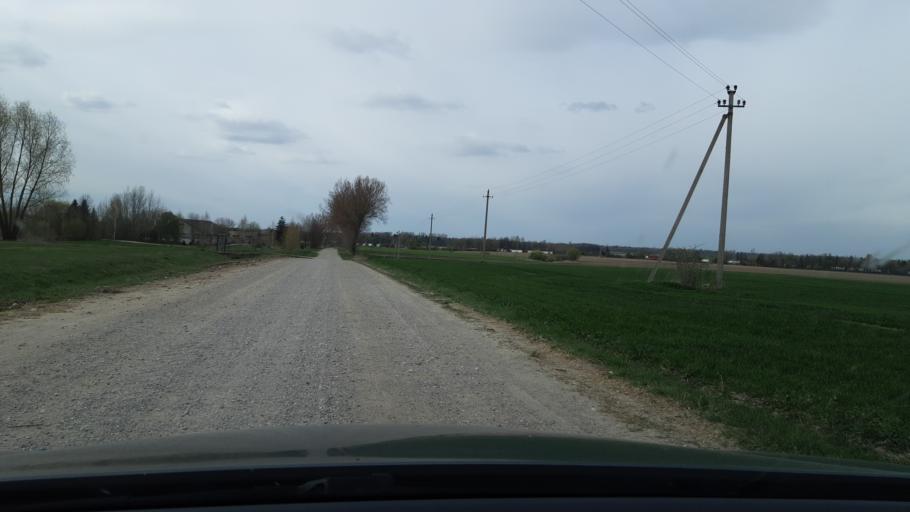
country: LT
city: Virbalis
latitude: 54.6173
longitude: 22.8414
